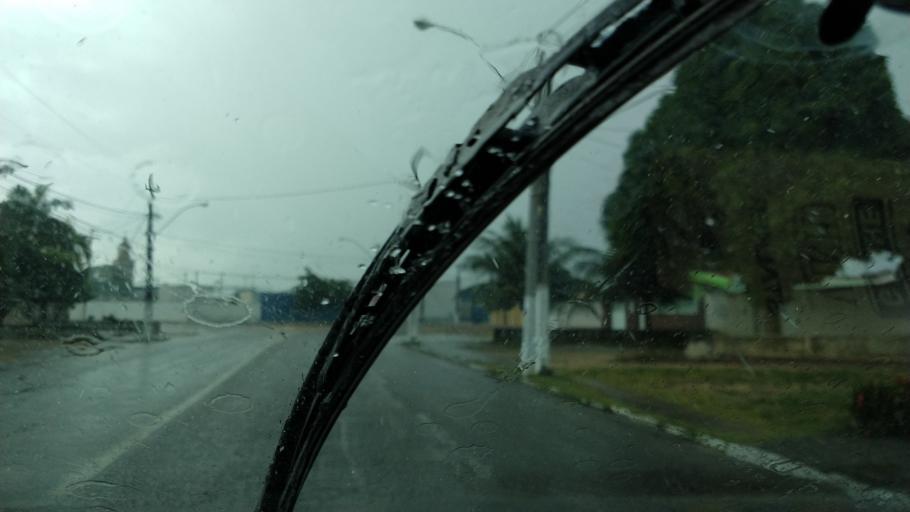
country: BR
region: Rio Grande do Norte
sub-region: Parnamirim
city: Parnamirim
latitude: -5.9225
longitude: -35.2670
